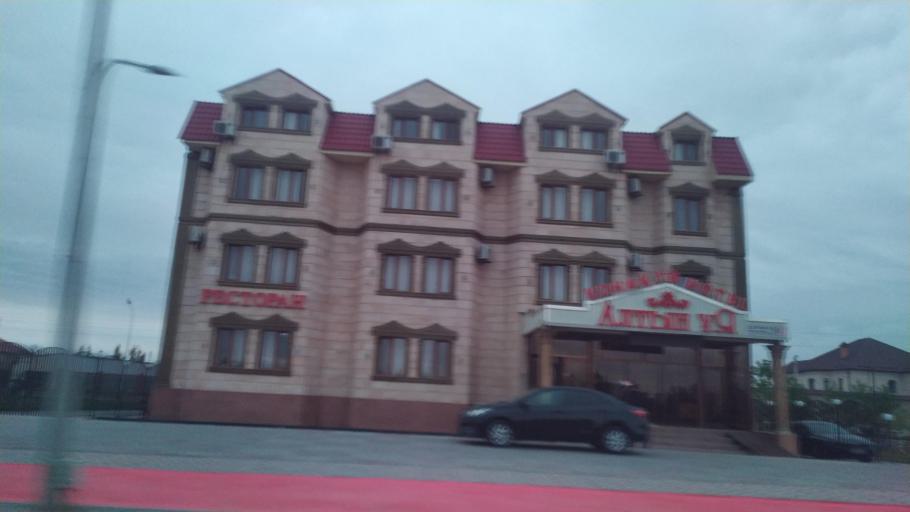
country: KZ
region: Ongtustik Qazaqstan
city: Turkestan
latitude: 43.2809
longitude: 68.3196
